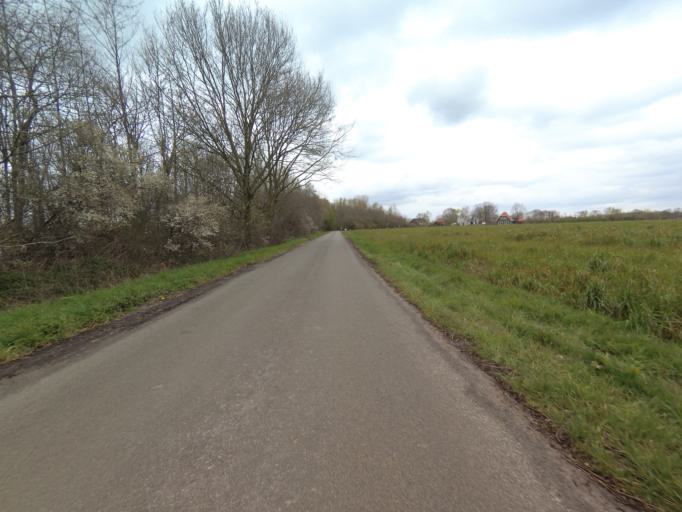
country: NL
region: Gelderland
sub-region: Gemeente Barneveld
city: Zwartebroek
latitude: 52.1600
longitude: 5.4866
